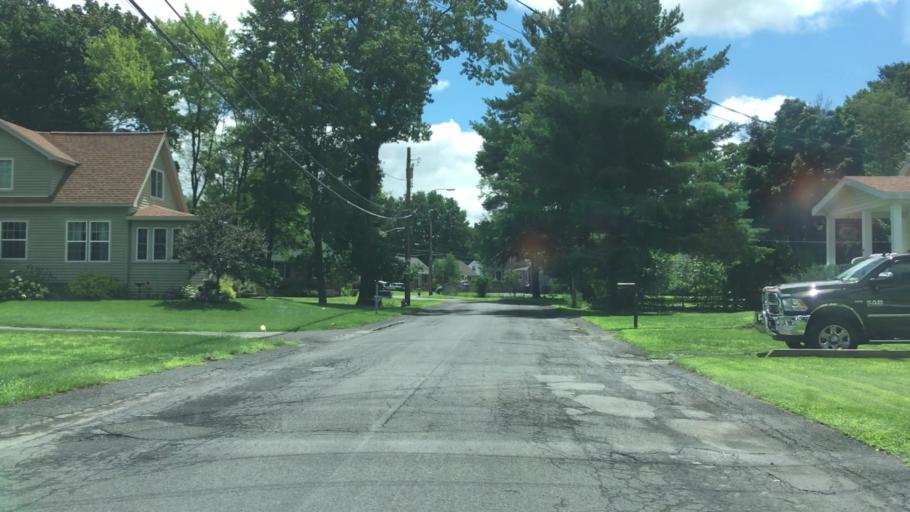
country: US
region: New York
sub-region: Albany County
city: Colonie
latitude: 42.7441
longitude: -73.8585
